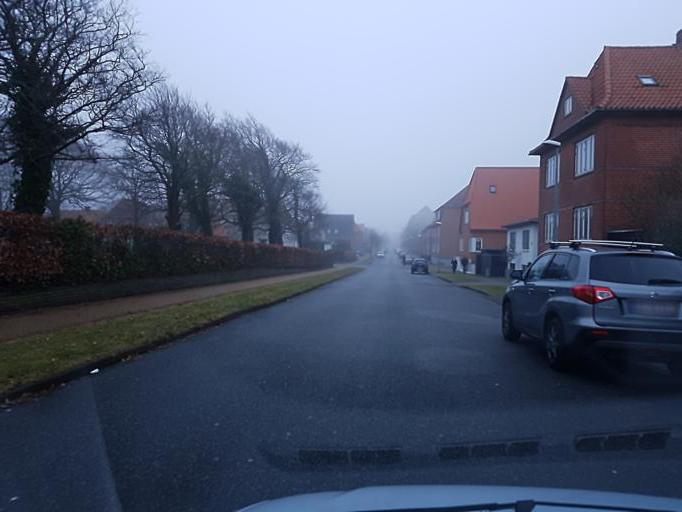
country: DK
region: South Denmark
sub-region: Esbjerg Kommune
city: Esbjerg
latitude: 55.4757
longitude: 8.4416
